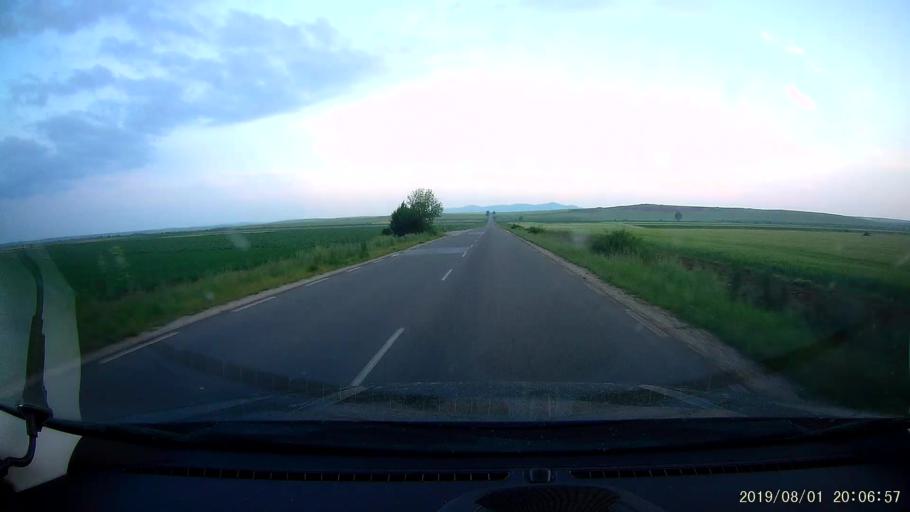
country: BG
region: Yambol
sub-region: Obshtina Yambol
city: Yambol
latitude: 42.5290
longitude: 26.5600
